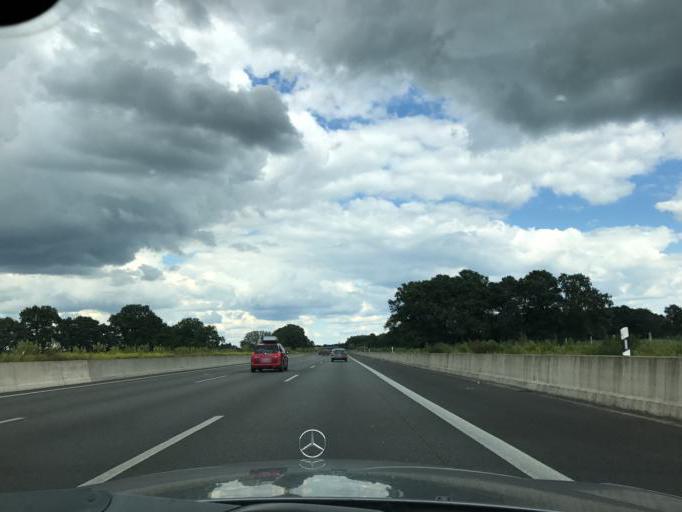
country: DE
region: Lower Saxony
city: Oyten
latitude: 53.0559
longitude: 9.0716
